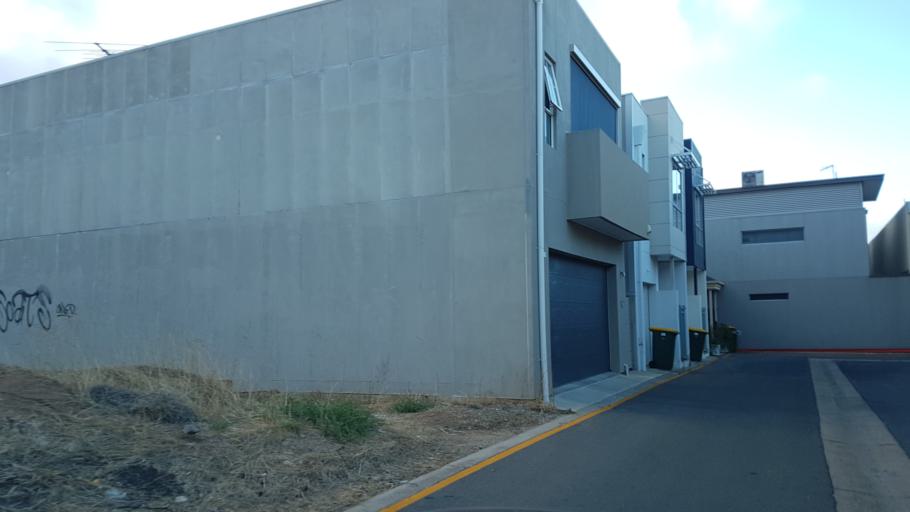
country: AU
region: South Australia
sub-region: Salisbury
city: Ingle Farm
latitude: -34.8063
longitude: 138.6116
